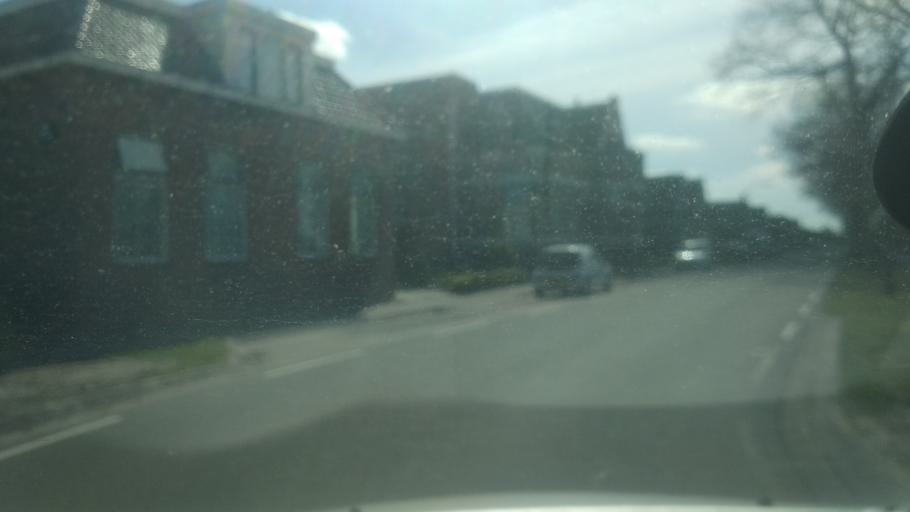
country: NL
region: Groningen
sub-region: Gemeente Stadskanaal
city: Stadskanaal
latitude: 52.9652
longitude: 6.9517
